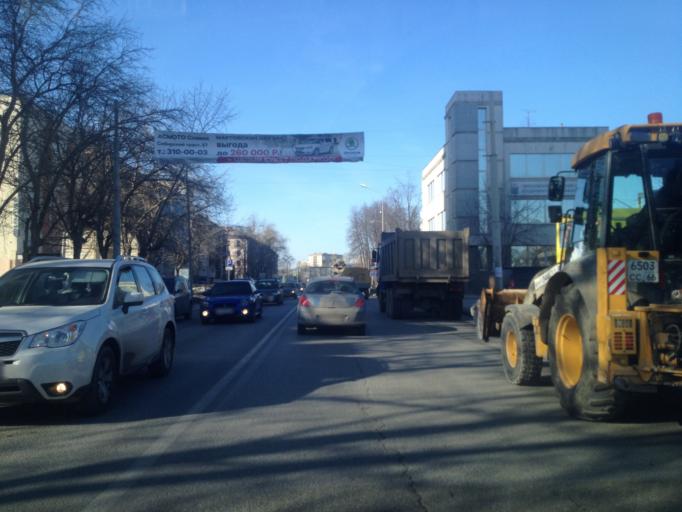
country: RU
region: Sverdlovsk
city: Yekaterinburg
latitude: 56.8423
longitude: 60.6318
